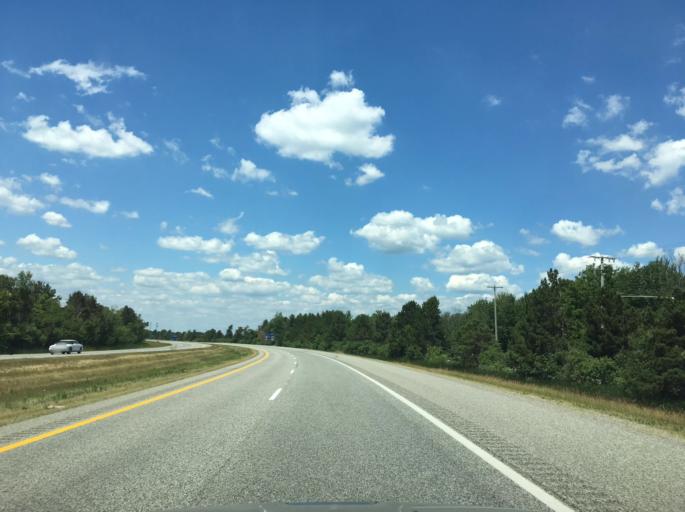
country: US
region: Michigan
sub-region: Midland County
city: Midland
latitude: 43.6552
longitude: -84.2091
